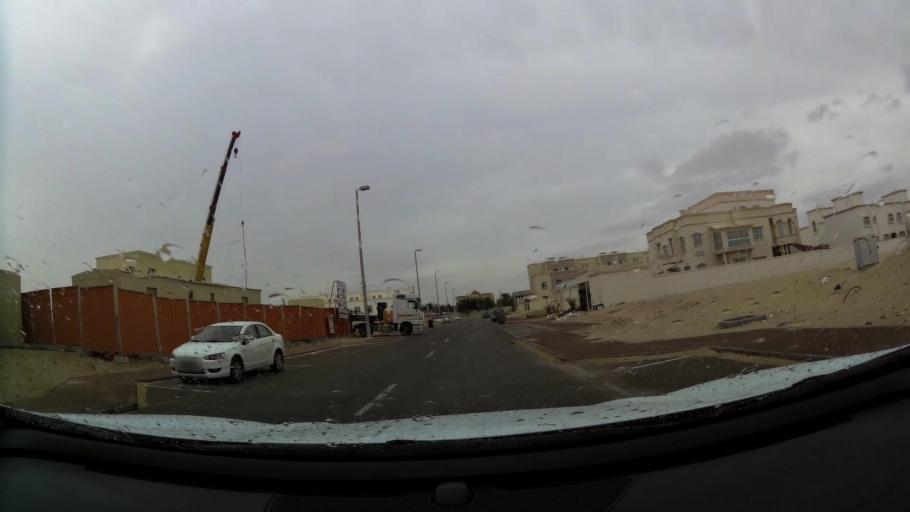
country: AE
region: Abu Dhabi
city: Abu Dhabi
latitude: 24.3607
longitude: 54.6435
